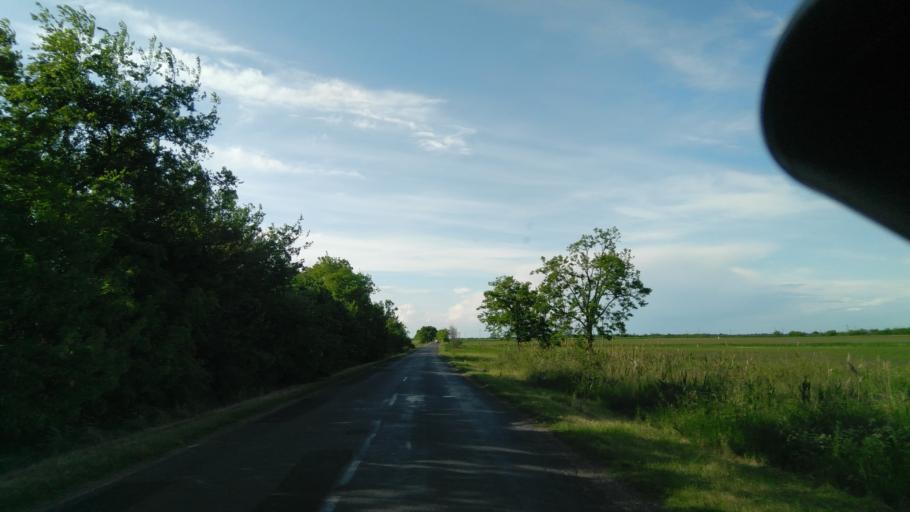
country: HU
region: Bekes
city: Lokoshaza
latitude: 46.4672
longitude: 21.2077
